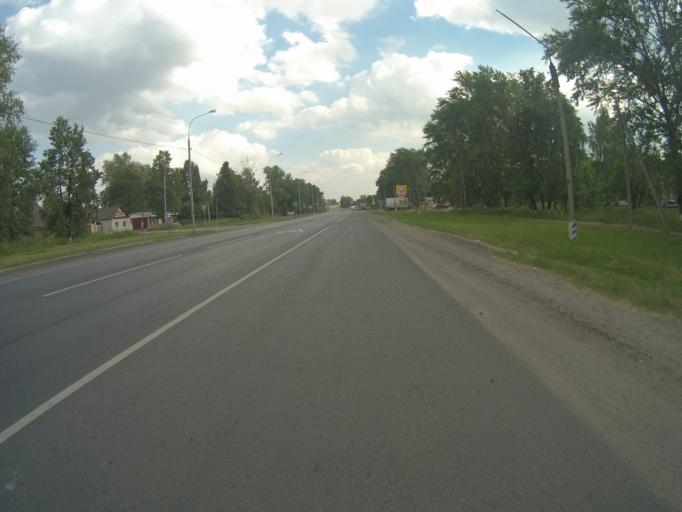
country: RU
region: Vladimir
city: Suzdal'
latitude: 56.3246
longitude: 40.4722
